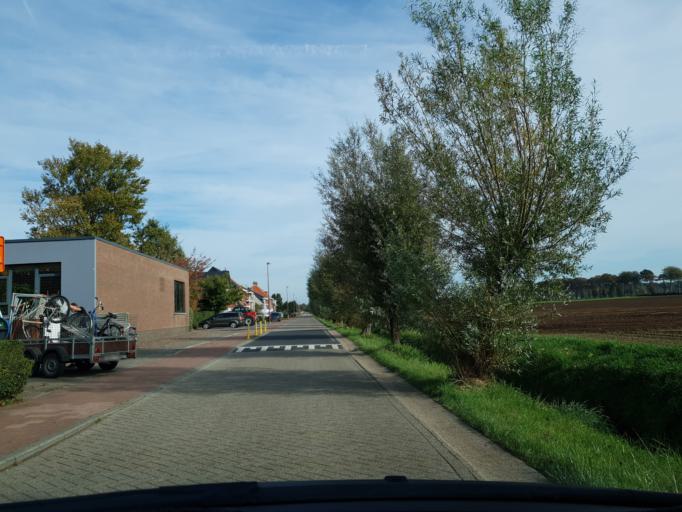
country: BE
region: Flanders
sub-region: Provincie Antwerpen
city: Stabroek
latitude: 51.3323
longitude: 4.3950
